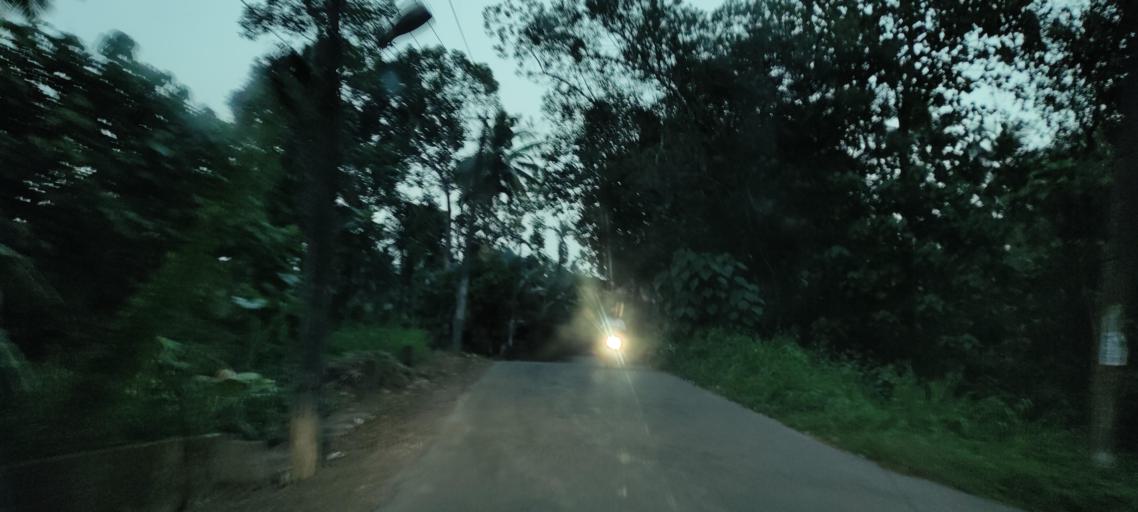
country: IN
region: Kerala
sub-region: Pattanamtitta
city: Adur
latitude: 9.1575
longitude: 76.7371
